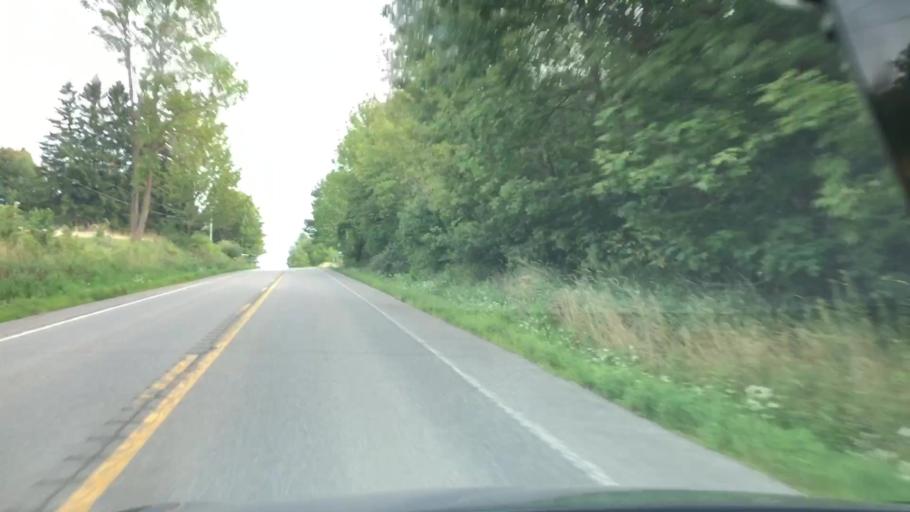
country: US
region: Pennsylvania
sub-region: Erie County
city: Union City
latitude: 41.8462
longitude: -79.8231
